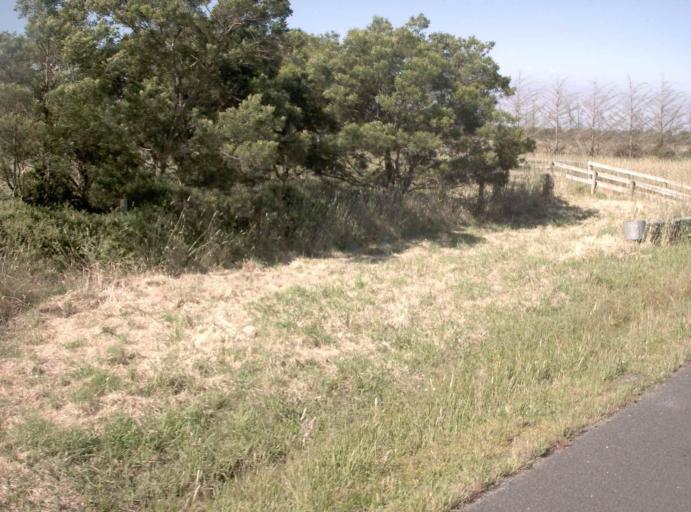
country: AU
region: Victoria
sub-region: Latrobe
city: Traralgon
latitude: -38.6250
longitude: 146.6341
